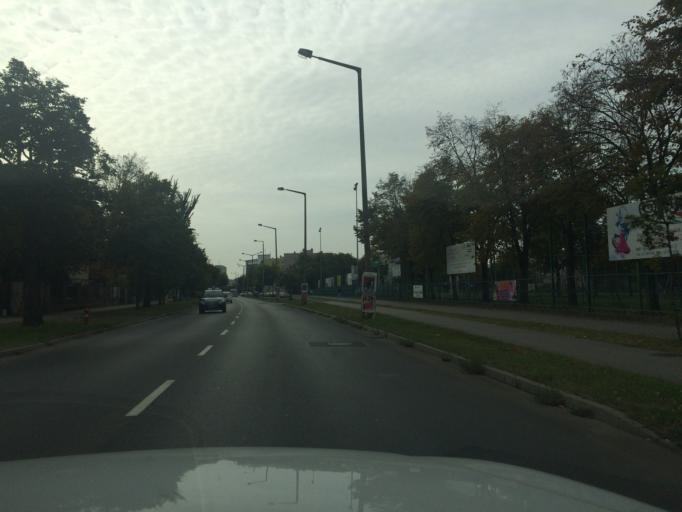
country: HU
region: Szabolcs-Szatmar-Bereg
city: Nyiregyhaza
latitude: 47.9702
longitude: 21.7154
